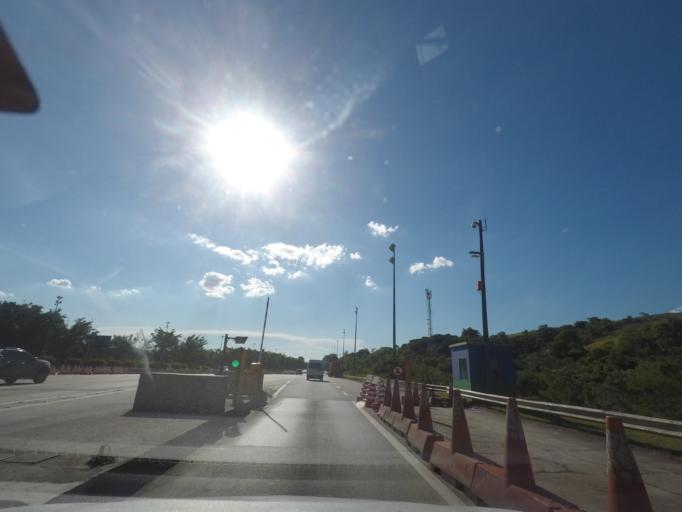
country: BR
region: Rio de Janeiro
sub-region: Petropolis
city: Petropolis
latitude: -22.6470
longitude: -43.1881
